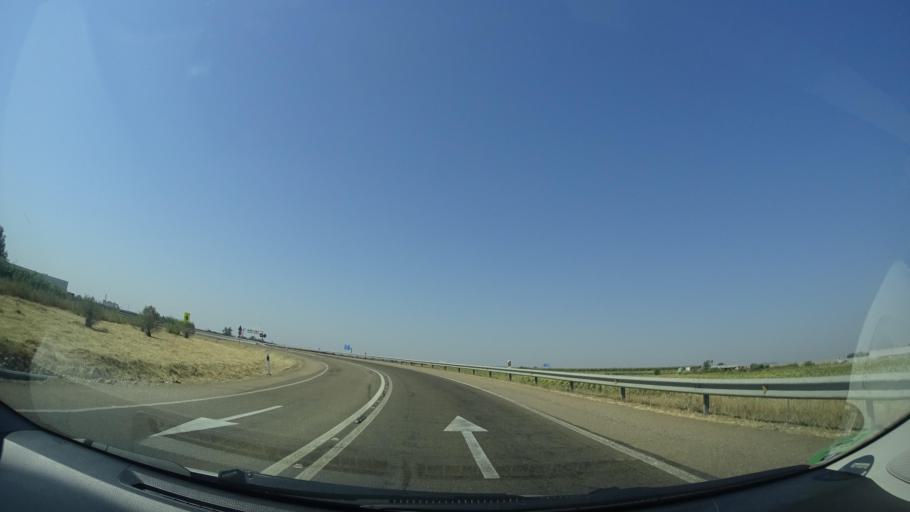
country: ES
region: Extremadura
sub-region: Provincia de Caceres
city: Miajadas
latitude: 39.1330
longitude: -5.9486
